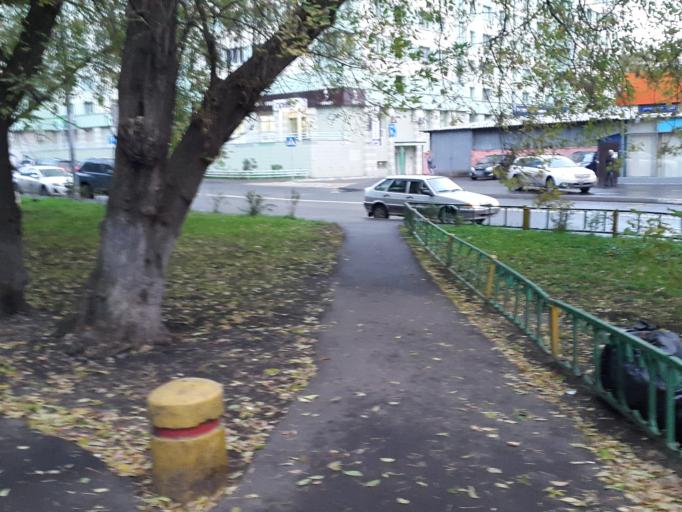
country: RU
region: Moscow
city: Pokrovskoye-Streshnevo
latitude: 55.8098
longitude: 37.4540
